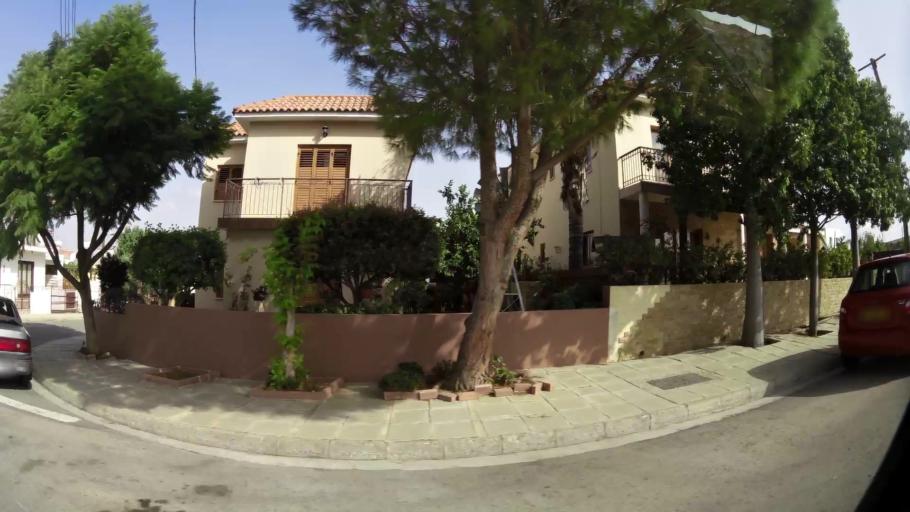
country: CY
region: Lefkosia
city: Dali
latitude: 35.0608
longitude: 33.3994
